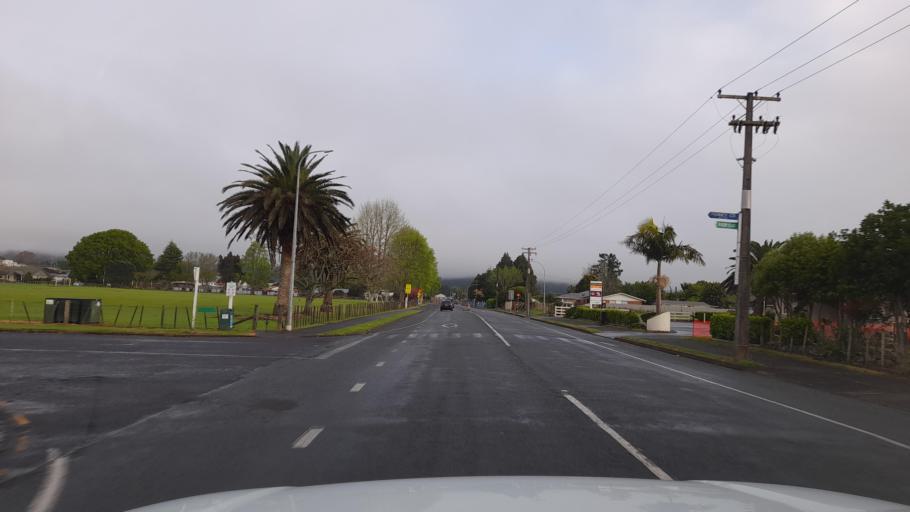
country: NZ
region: Northland
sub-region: Far North District
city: Waimate North
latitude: -35.4119
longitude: 173.8067
